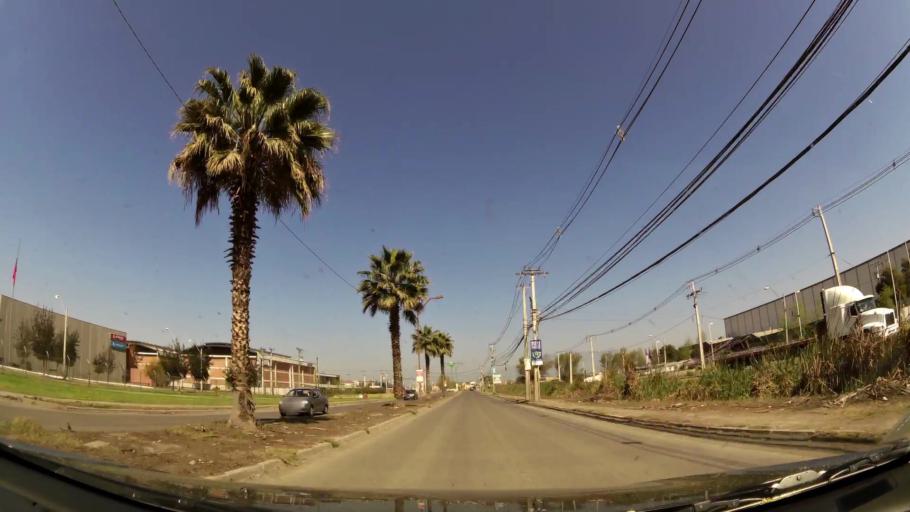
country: CL
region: Santiago Metropolitan
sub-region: Provincia de Chacabuco
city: Chicureo Abajo
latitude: -33.3225
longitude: -70.7393
